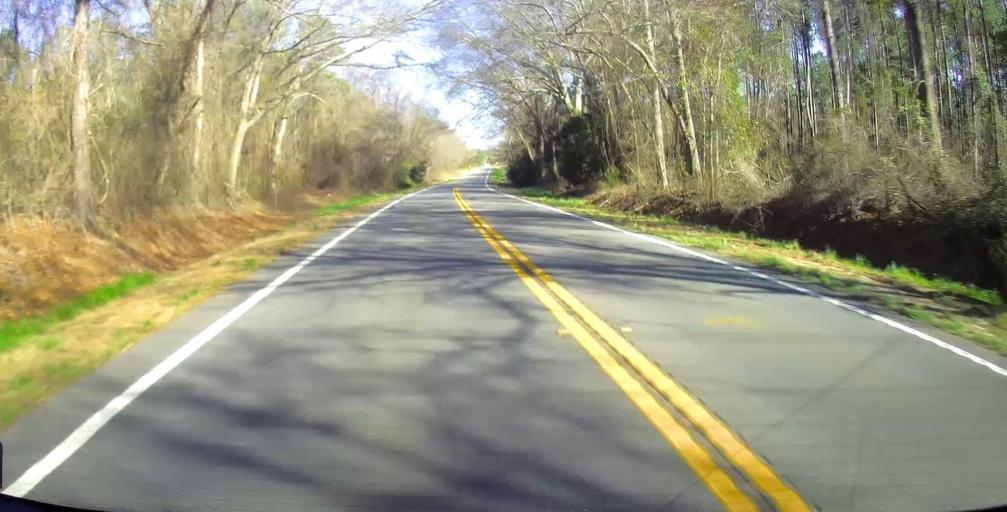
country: US
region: Georgia
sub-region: Macon County
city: Oglethorpe
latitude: 32.3515
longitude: -84.1571
